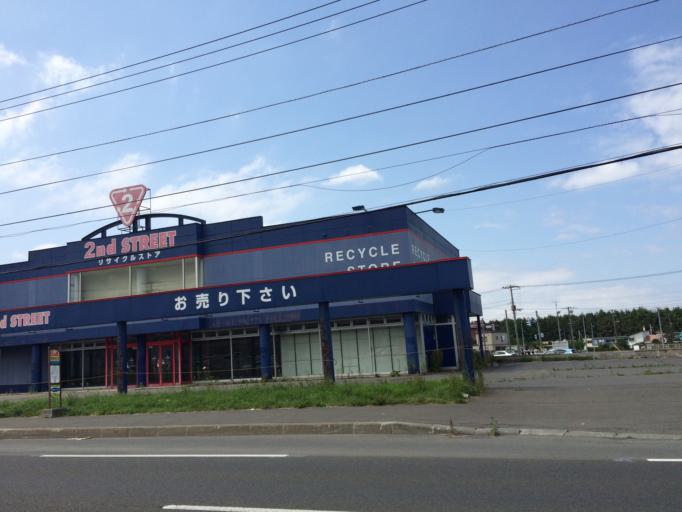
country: JP
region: Hokkaido
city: Ebetsu
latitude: 43.0479
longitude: 141.4800
